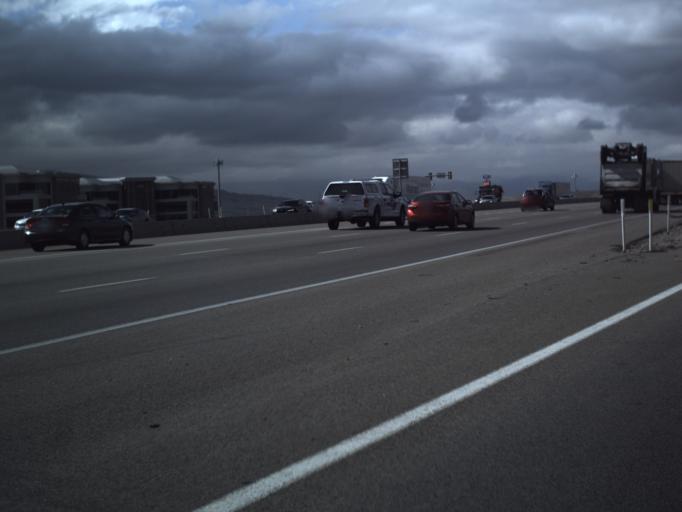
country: US
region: Utah
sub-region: Utah County
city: Lehi
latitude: 40.4280
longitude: -111.8870
